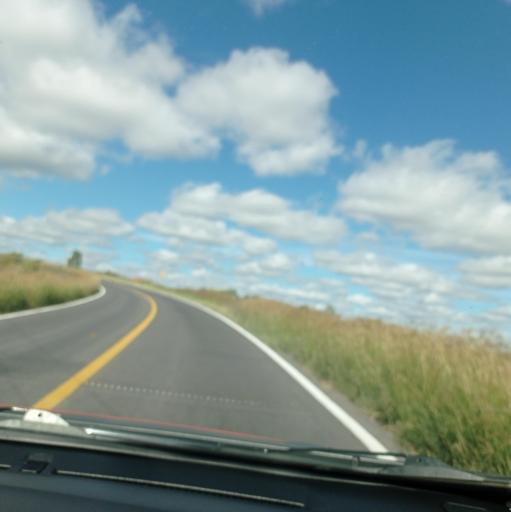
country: MX
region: Jalisco
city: San Diego de Alejandria
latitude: 21.0080
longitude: -102.0118
